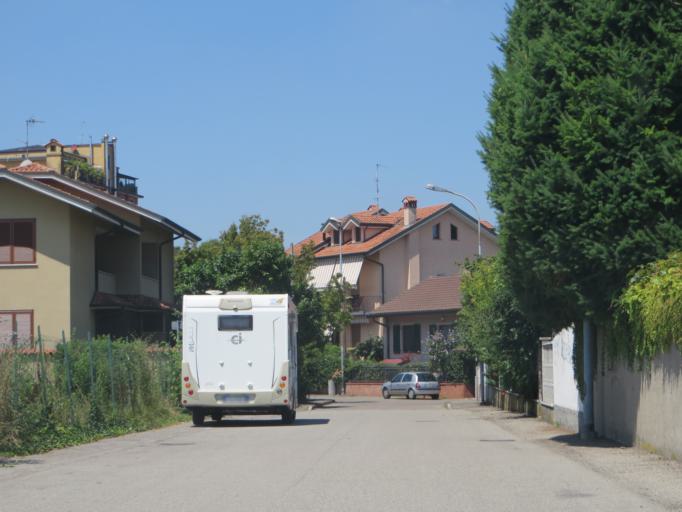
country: IT
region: Lombardy
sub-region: Citta metropolitana di Milano
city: Bareggio
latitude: 45.4736
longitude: 8.9929
